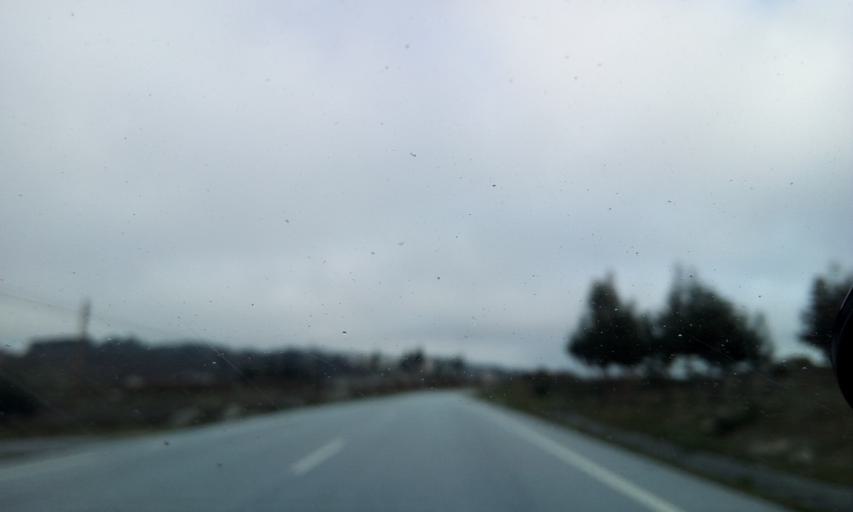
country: PT
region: Guarda
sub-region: Fornos de Algodres
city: Fornos de Algodres
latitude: 40.6723
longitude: -7.4736
